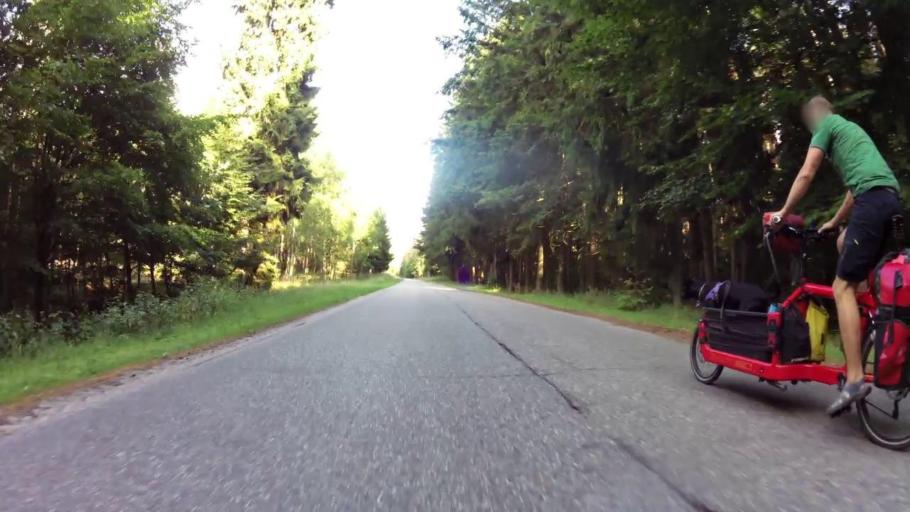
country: PL
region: West Pomeranian Voivodeship
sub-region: Powiat drawski
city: Drawsko Pomorskie
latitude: 53.4655
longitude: 15.8479
